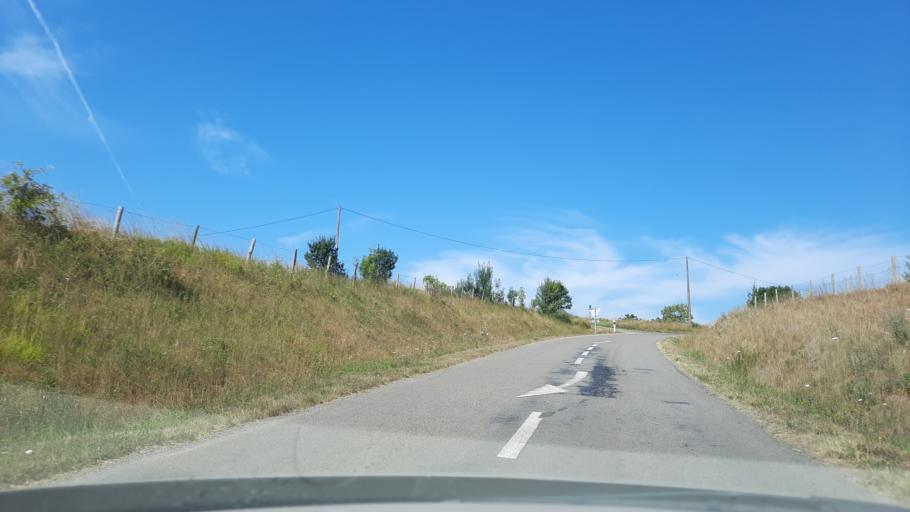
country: FR
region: Midi-Pyrenees
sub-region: Departement de l'Aveyron
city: Montbazens
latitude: 44.4944
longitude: 2.2286
